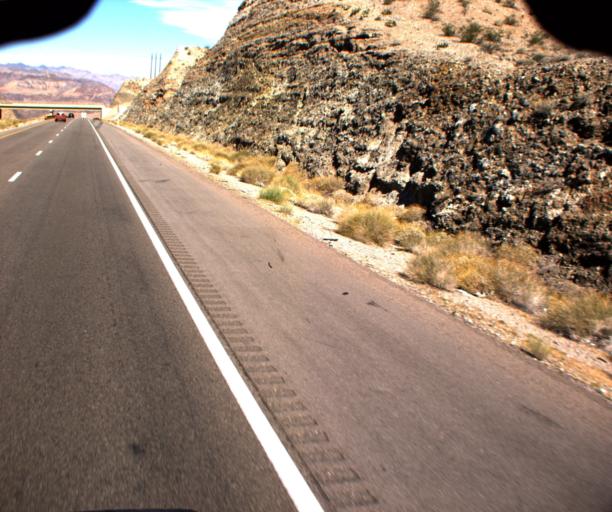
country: US
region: Nevada
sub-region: Clark County
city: Boulder City
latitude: 35.9695
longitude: -114.6793
